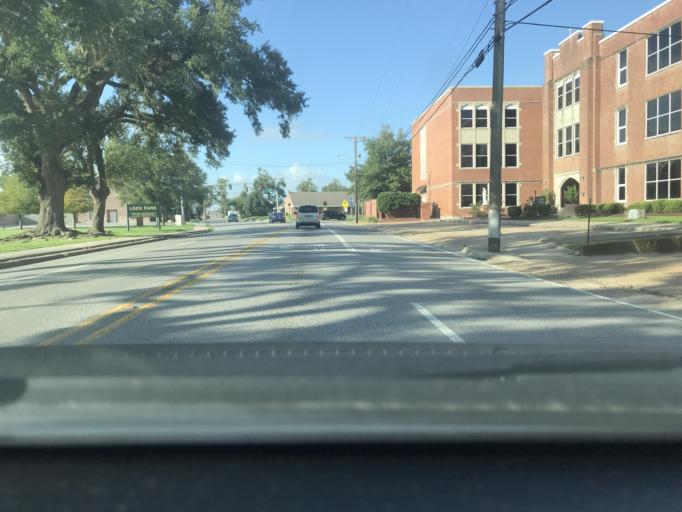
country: US
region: Louisiana
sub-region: Calcasieu Parish
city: Lake Charles
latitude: 30.2200
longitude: -93.2191
